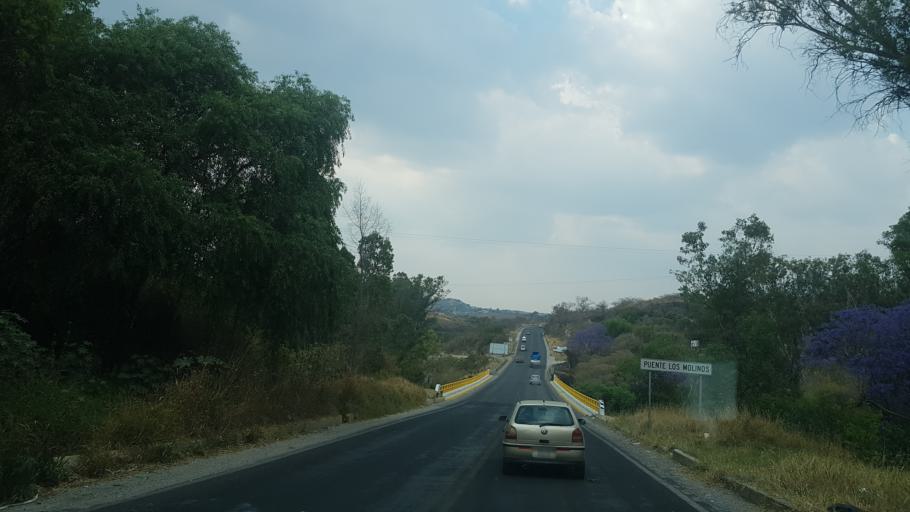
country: MX
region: Puebla
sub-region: Santa Isabel Cholula
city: Santa Ana Acozautla
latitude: 18.9481
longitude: -98.3888
